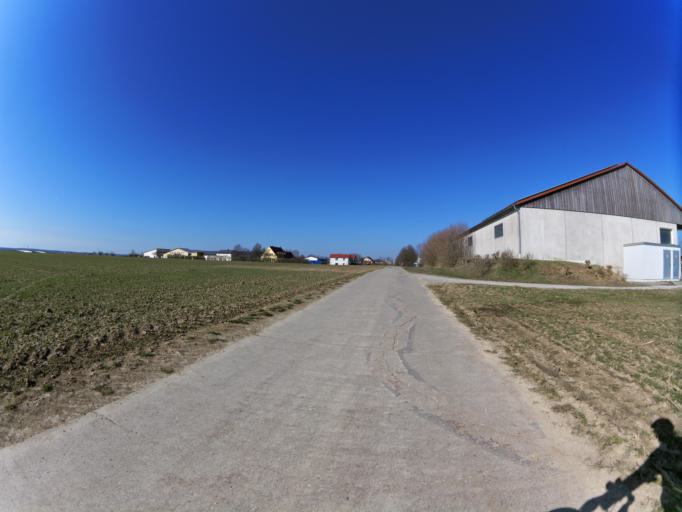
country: DE
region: Bavaria
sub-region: Regierungsbezirk Unterfranken
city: Bergtheim
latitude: 49.8909
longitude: 10.0699
